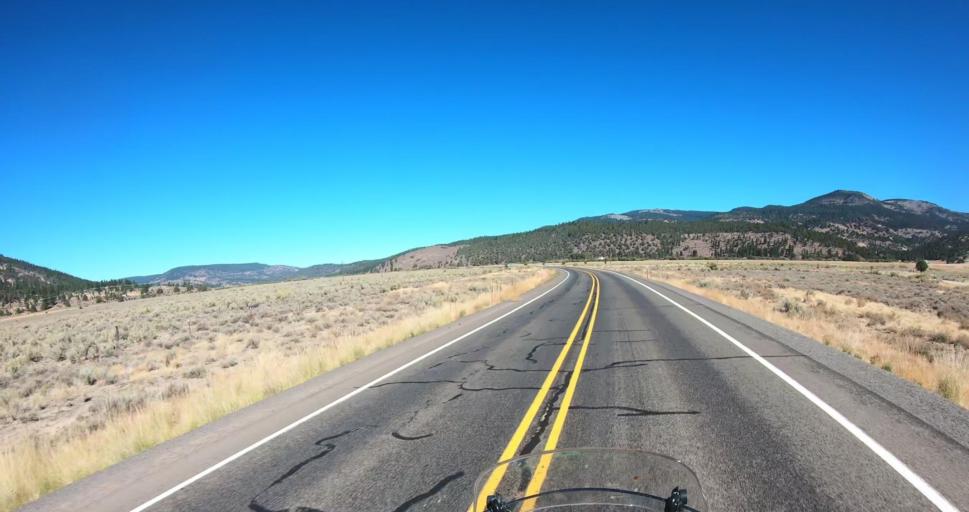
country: US
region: Oregon
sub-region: Lake County
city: Lakeview
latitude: 42.3300
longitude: -120.2998
